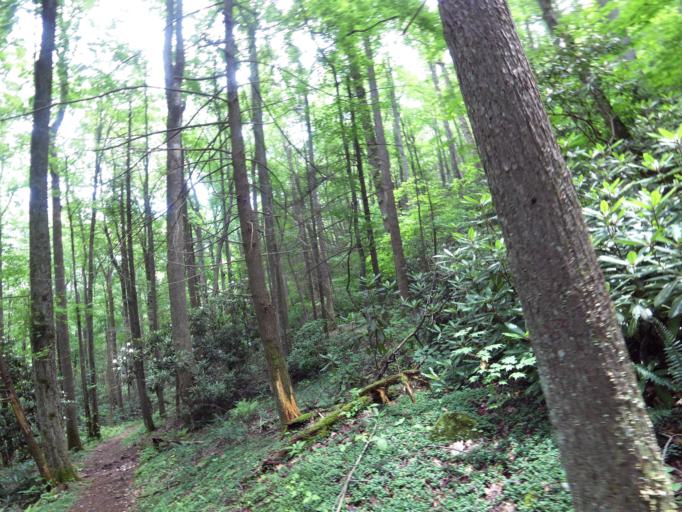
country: US
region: Tennessee
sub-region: Blount County
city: Wildwood
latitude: 35.5988
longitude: -83.7408
